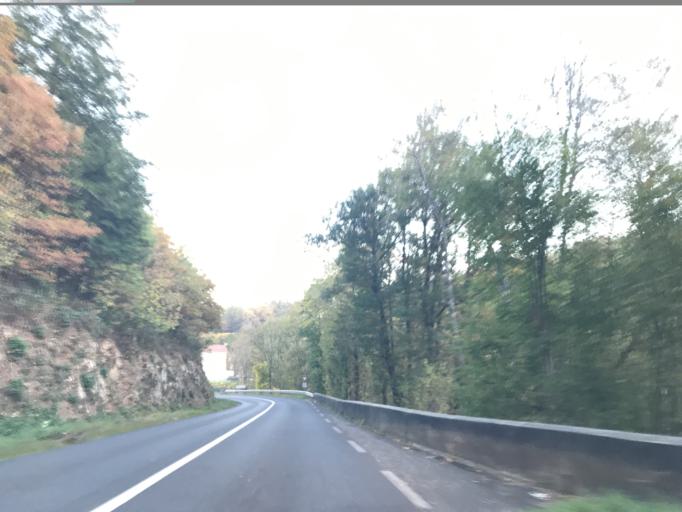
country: FR
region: Auvergne
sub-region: Departement du Puy-de-Dome
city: Celles-sur-Durolle
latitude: 45.8657
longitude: 3.6388
